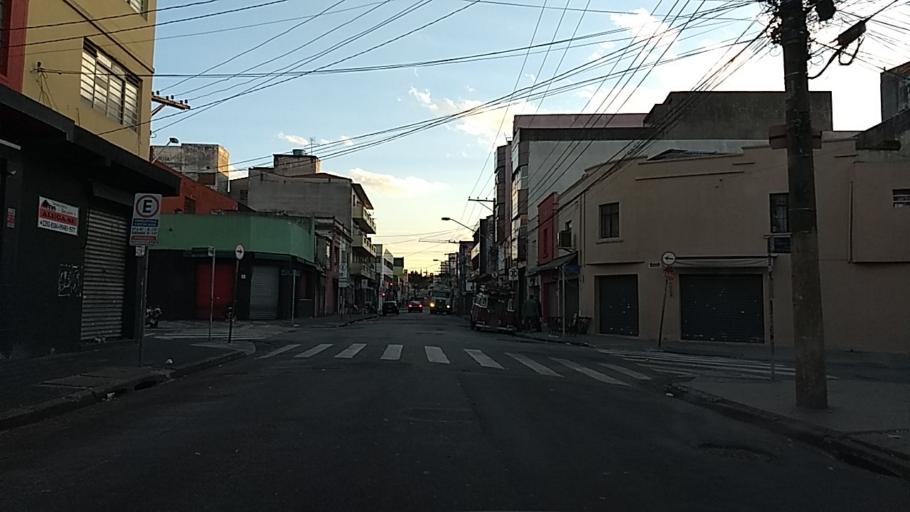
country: BR
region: Sao Paulo
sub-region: Sao Paulo
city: Sao Paulo
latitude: -23.5386
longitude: -46.6152
